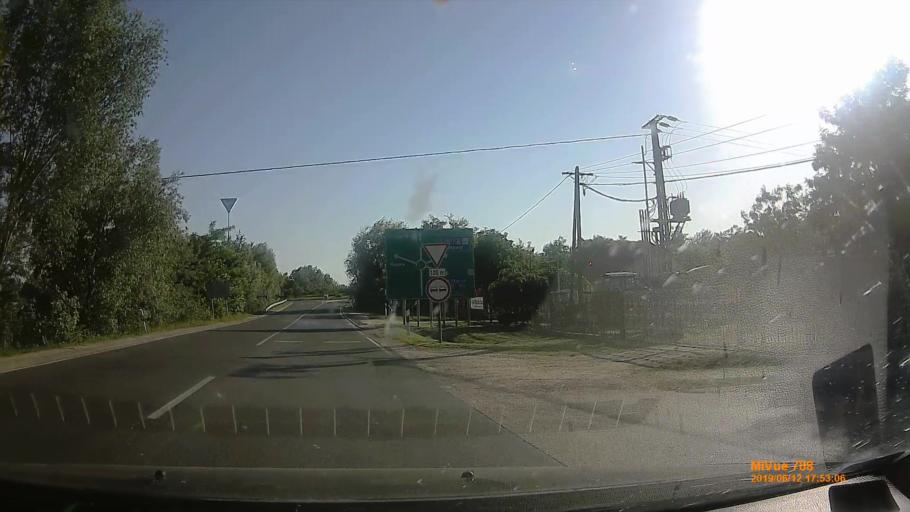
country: HU
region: Csongrad
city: Roszke
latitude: 46.1914
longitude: 20.0003
